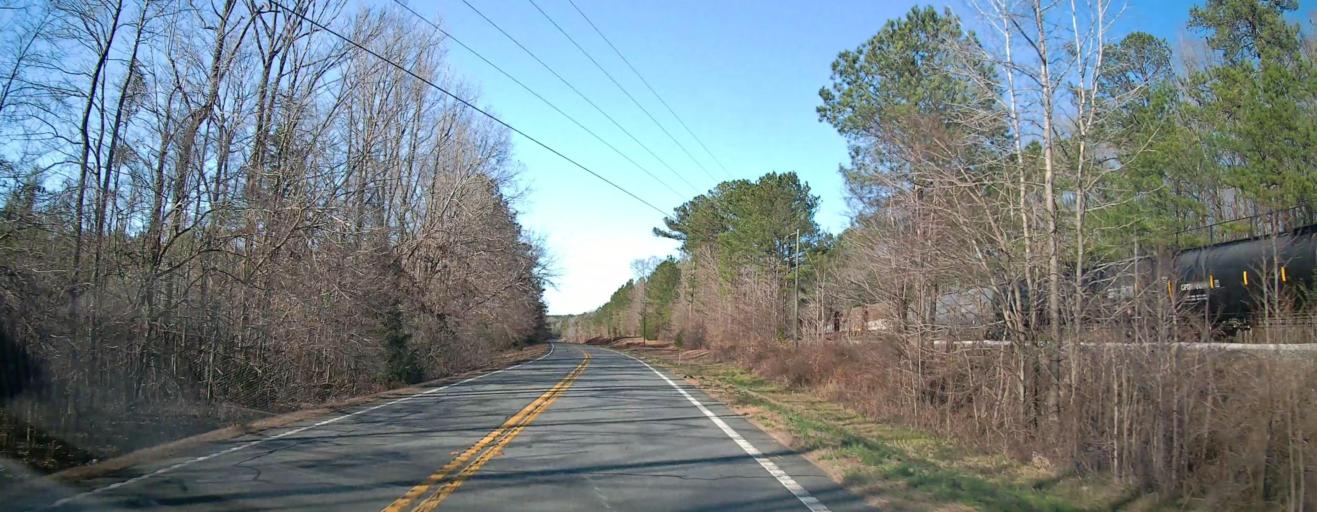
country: US
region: Georgia
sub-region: Talbot County
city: Talbotton
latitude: 32.7358
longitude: -84.5543
